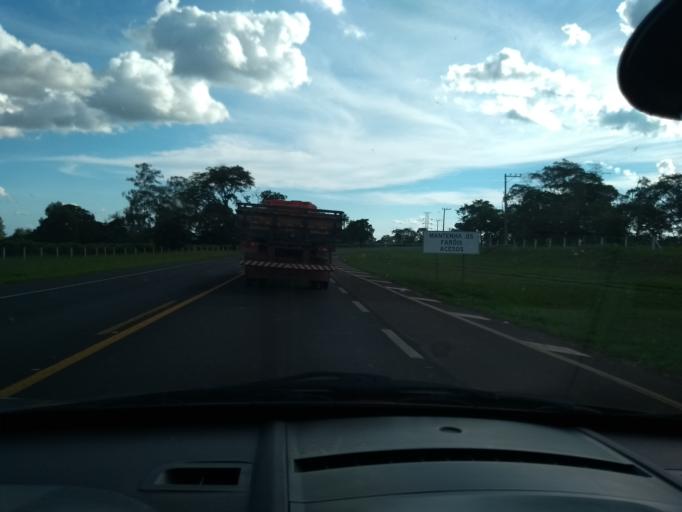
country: BR
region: Sao Paulo
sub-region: Casa Branca
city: Casa Branca
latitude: -21.7964
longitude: -47.0750
